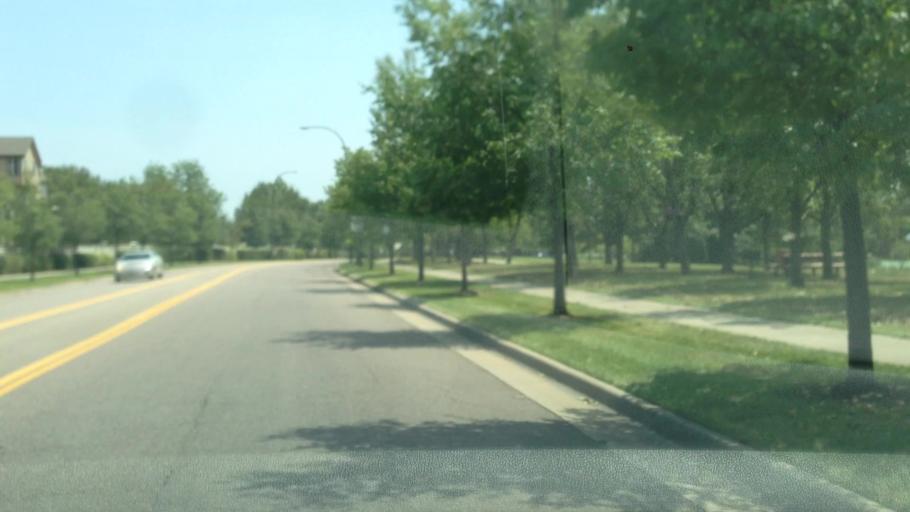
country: US
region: Colorado
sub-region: Jefferson County
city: Columbine
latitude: 39.6144
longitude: -105.0597
